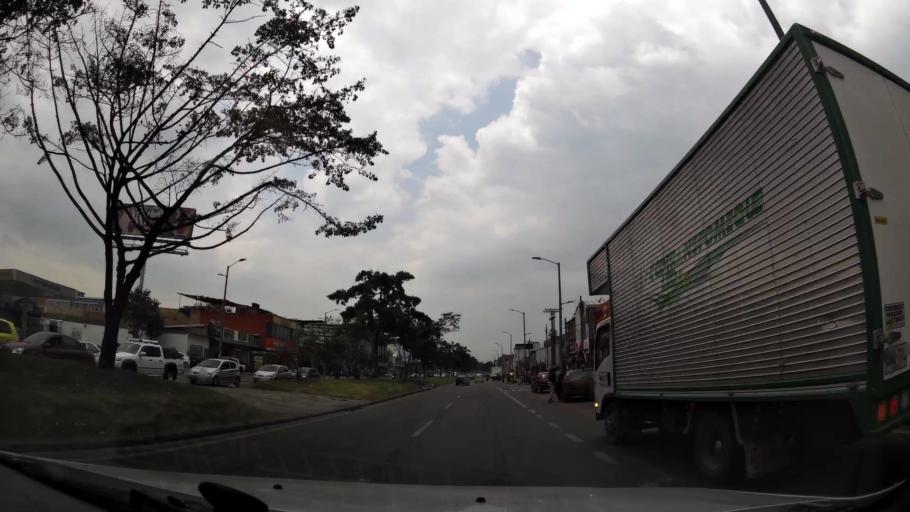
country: CO
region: Bogota D.C.
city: Bogota
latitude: 4.5899
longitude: -74.1094
